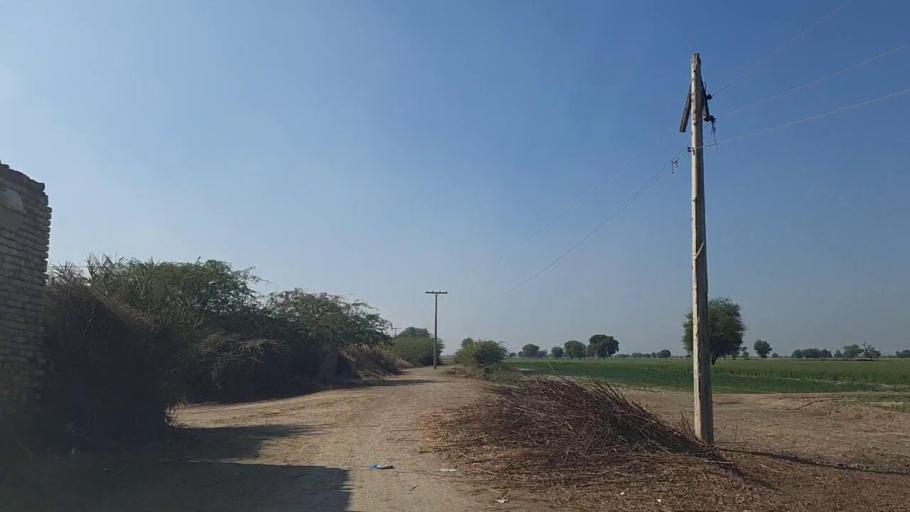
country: PK
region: Sindh
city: Shahpur Chakar
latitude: 26.1956
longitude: 68.6097
